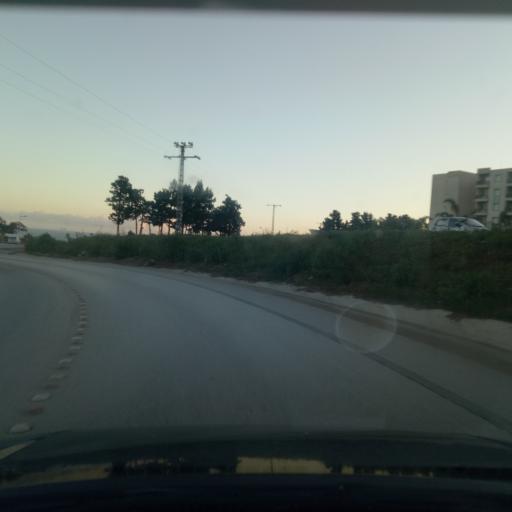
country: DZ
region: Tipaza
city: Bou Ismail
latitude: 36.6440
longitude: 2.7120
